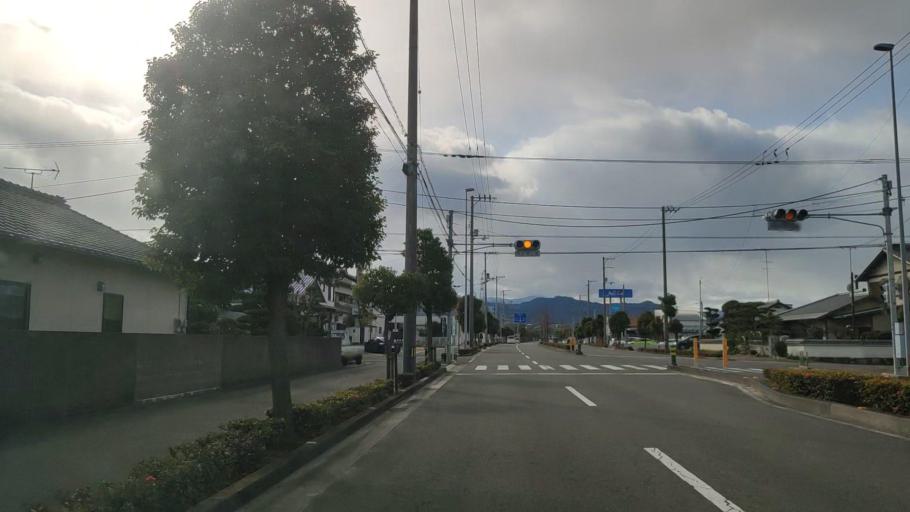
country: JP
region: Ehime
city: Saijo
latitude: 34.0428
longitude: 133.0030
